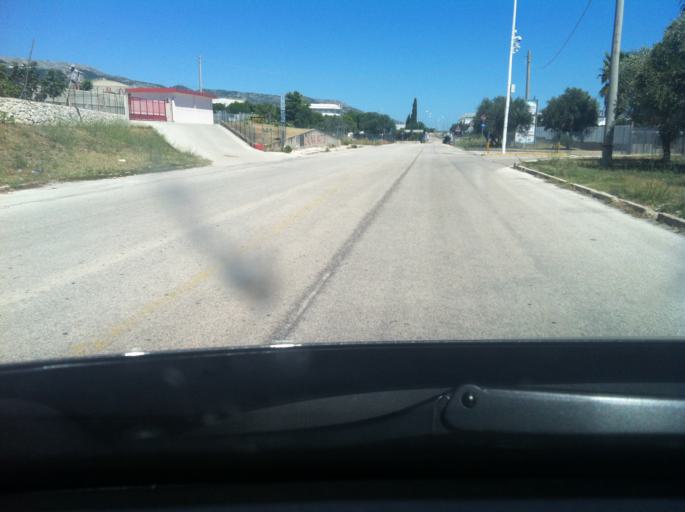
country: IT
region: Apulia
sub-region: Provincia di Foggia
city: Manfredonia
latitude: 41.6462
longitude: 15.9361
